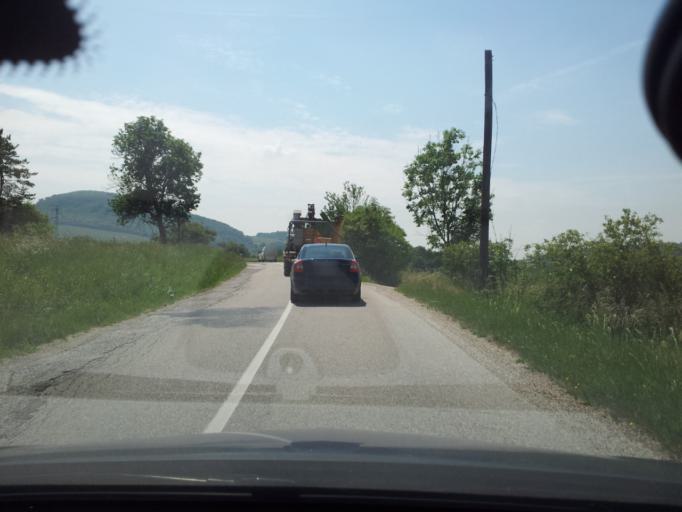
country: SK
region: Nitriansky
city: Partizanske
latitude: 48.5128
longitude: 18.4303
